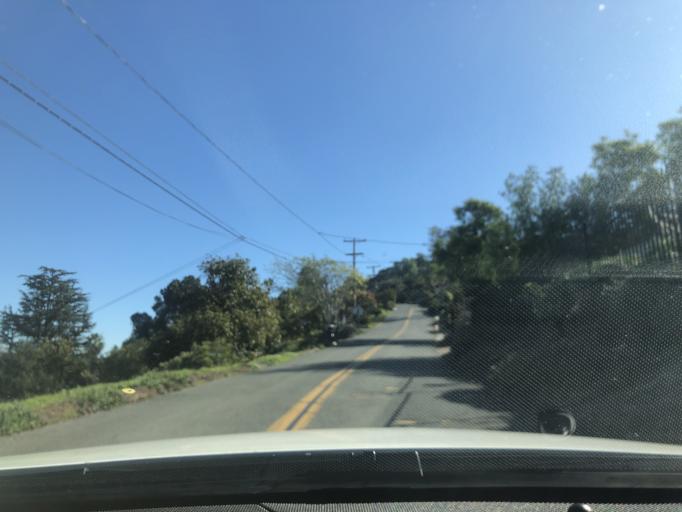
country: US
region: California
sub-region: San Diego County
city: El Cajon
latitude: 32.7838
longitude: -116.9418
